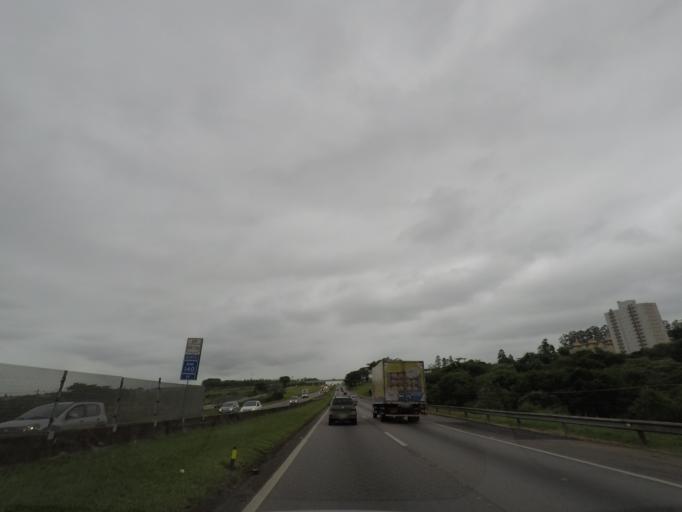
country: BR
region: Sao Paulo
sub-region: Sao Jose Dos Campos
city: Sao Jose dos Campos
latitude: -23.1645
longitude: -45.8101
